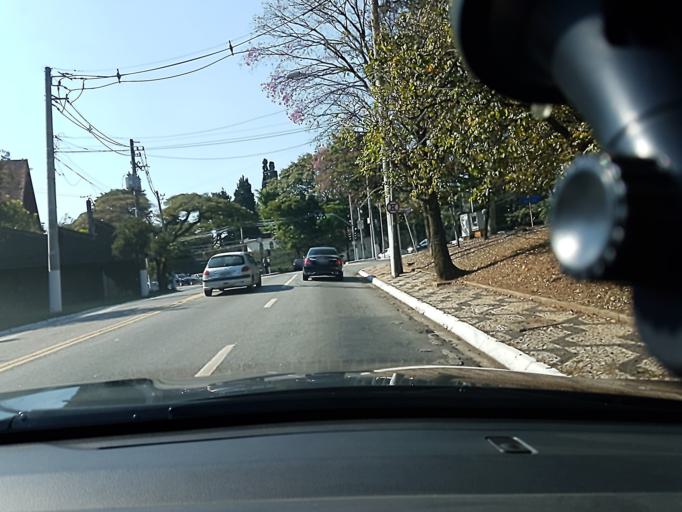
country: BR
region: Sao Paulo
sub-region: Taboao Da Serra
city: Taboao da Serra
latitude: -23.5996
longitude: -46.7089
